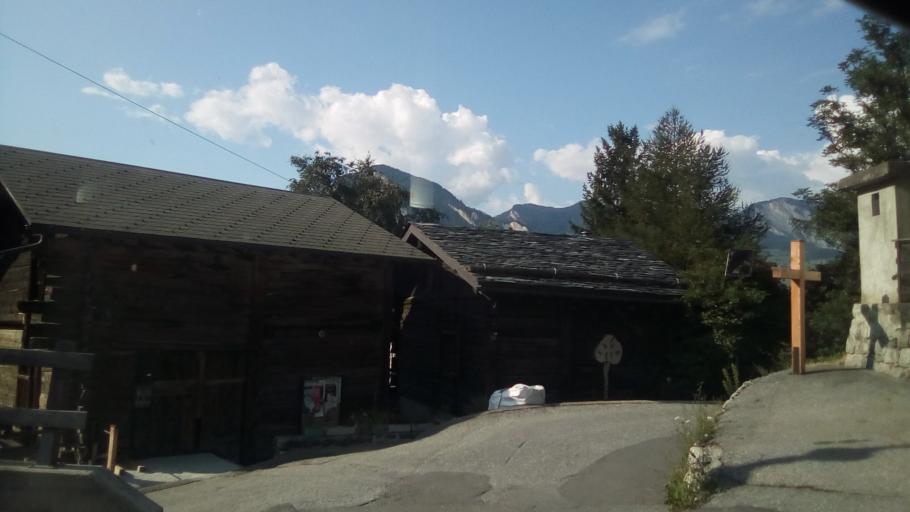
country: CH
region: Valais
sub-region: Entremont District
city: Orsieres
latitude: 46.0568
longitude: 7.1541
